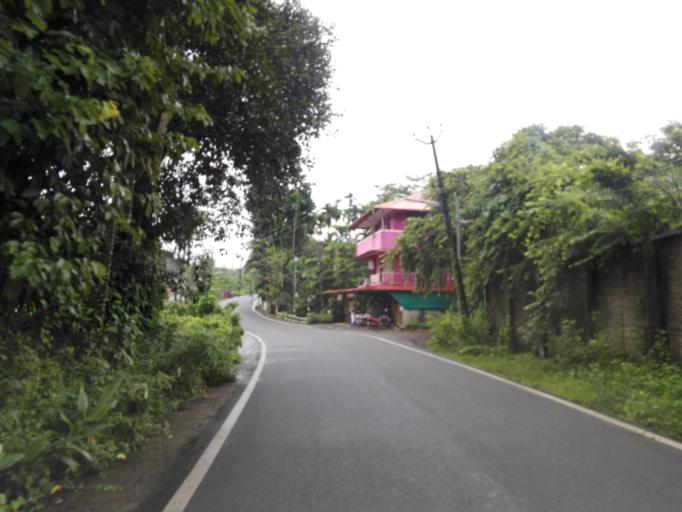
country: IN
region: Kerala
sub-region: Ernakulam
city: Aluva
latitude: 10.0535
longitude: 76.3609
